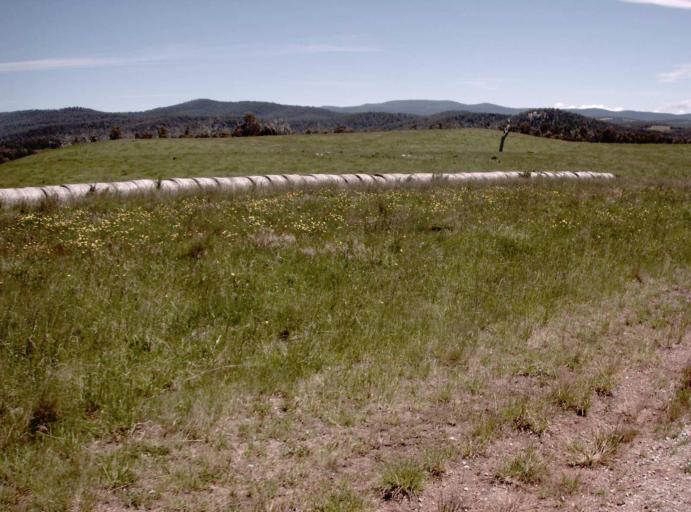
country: AU
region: New South Wales
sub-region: Snowy River
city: Jindabyne
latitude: -37.0883
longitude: 148.2572
